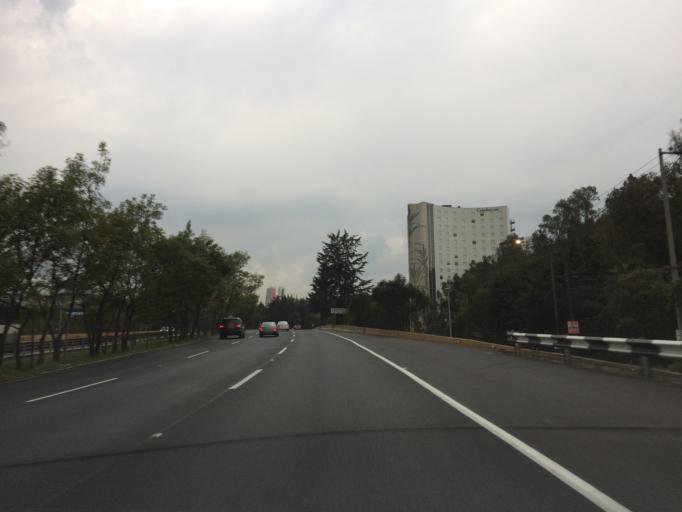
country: MX
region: Mexico City
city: Col. Bosques de las Lomas
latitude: 19.3761
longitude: -99.2593
